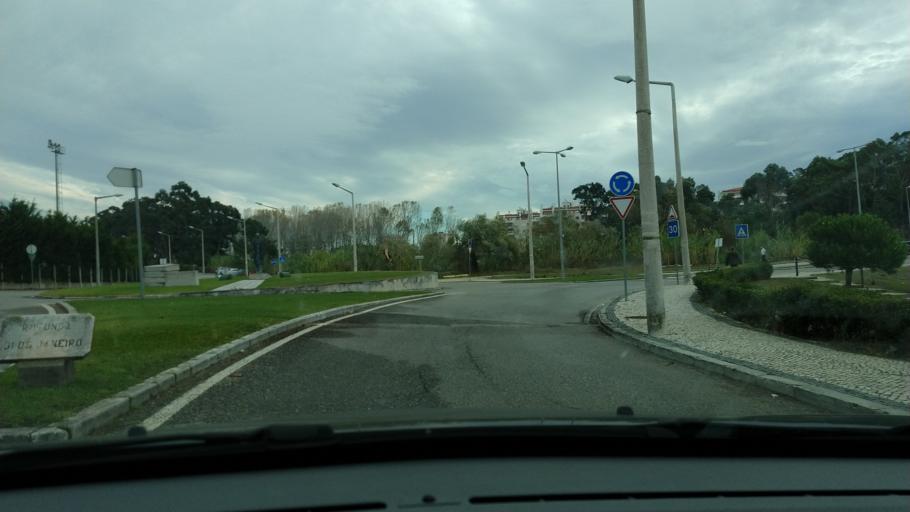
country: PT
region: Coimbra
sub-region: Figueira da Foz
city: Figueira da Foz
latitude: 40.1598
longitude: -8.8586
